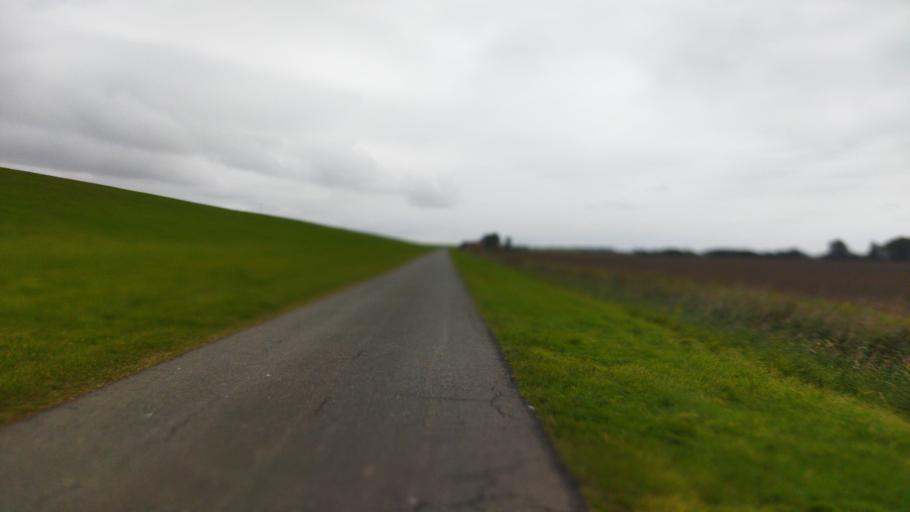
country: NL
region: Groningen
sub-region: Gemeente Delfzijl
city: Delfzijl
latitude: 53.4515
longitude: 7.0231
